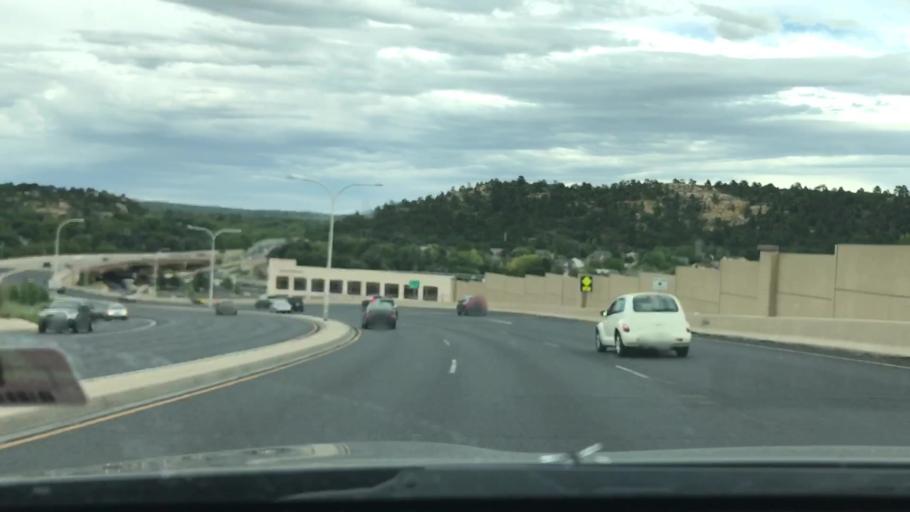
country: US
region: Colorado
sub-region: El Paso County
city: Colorado Springs
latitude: 38.8876
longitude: -104.7899
